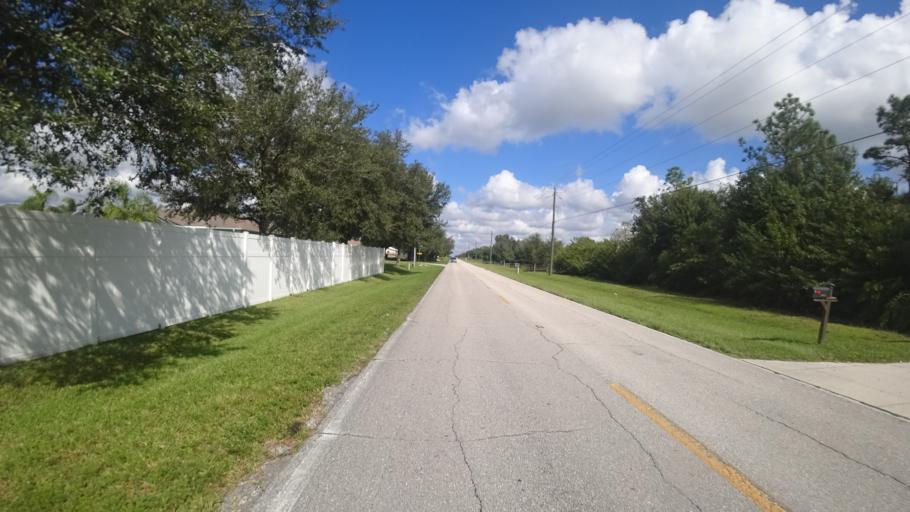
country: US
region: Florida
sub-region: Sarasota County
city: Lake Sarasota
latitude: 27.3942
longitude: -82.2712
